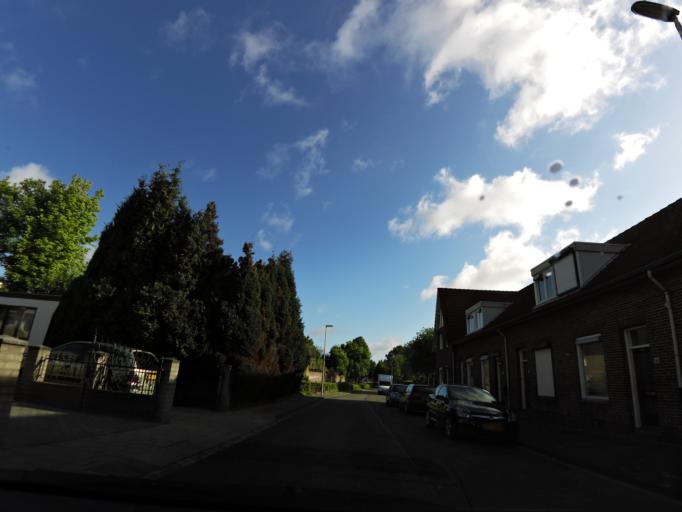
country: NL
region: Limburg
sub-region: Gemeente Voerendaal
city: Ubachsberg
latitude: 50.8731
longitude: 5.9604
